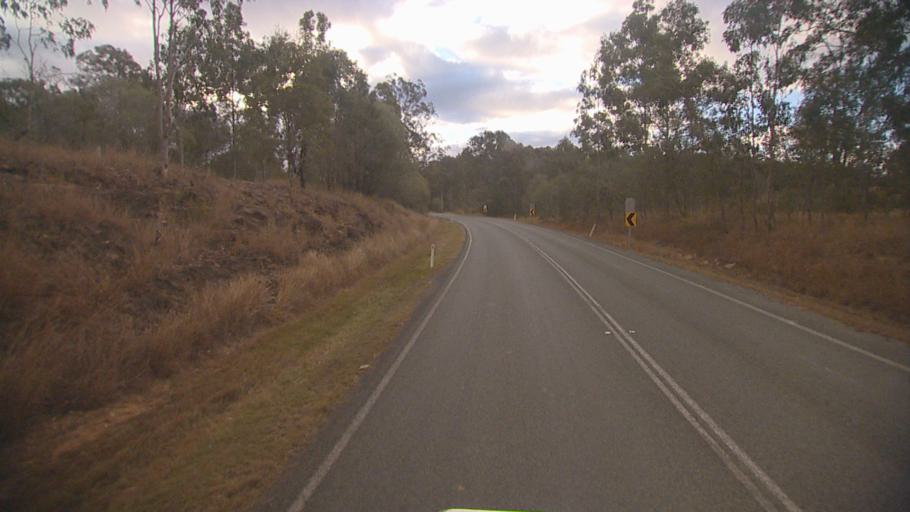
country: AU
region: Queensland
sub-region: Logan
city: Cedar Vale
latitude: -27.8942
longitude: 153.0876
